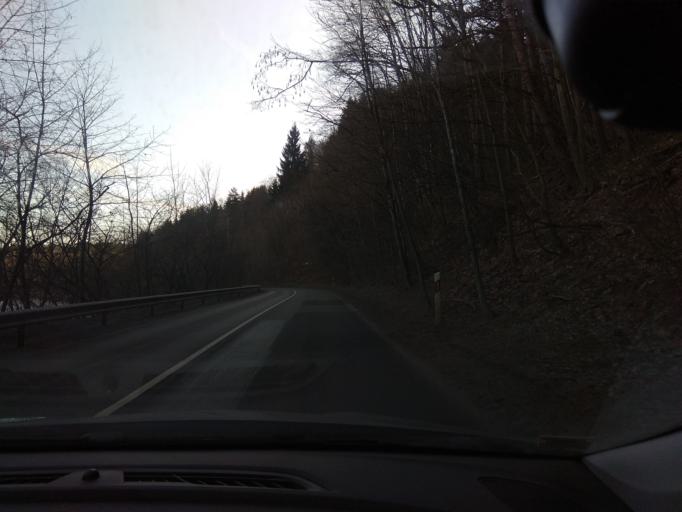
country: LT
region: Vilnius County
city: Lazdynai
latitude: 54.6588
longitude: 25.1754
